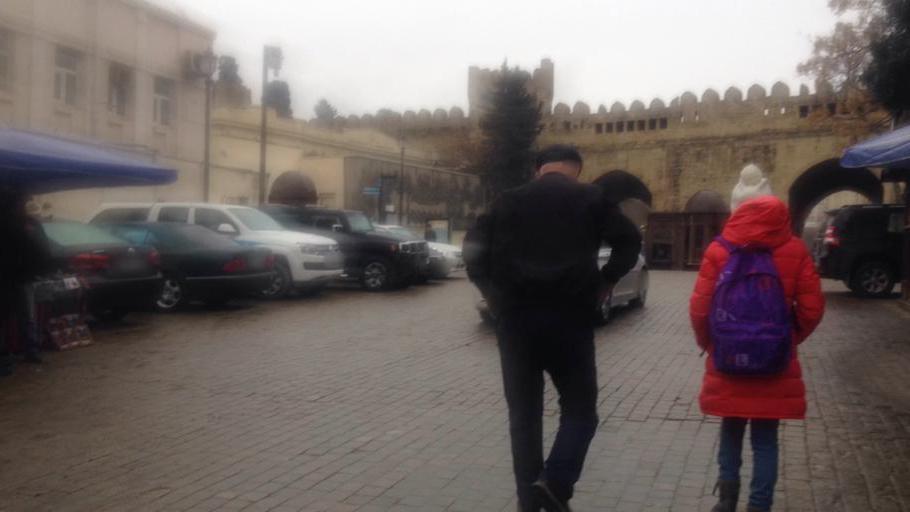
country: AZ
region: Baki
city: Badamdar
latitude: 40.3683
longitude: 49.8365
